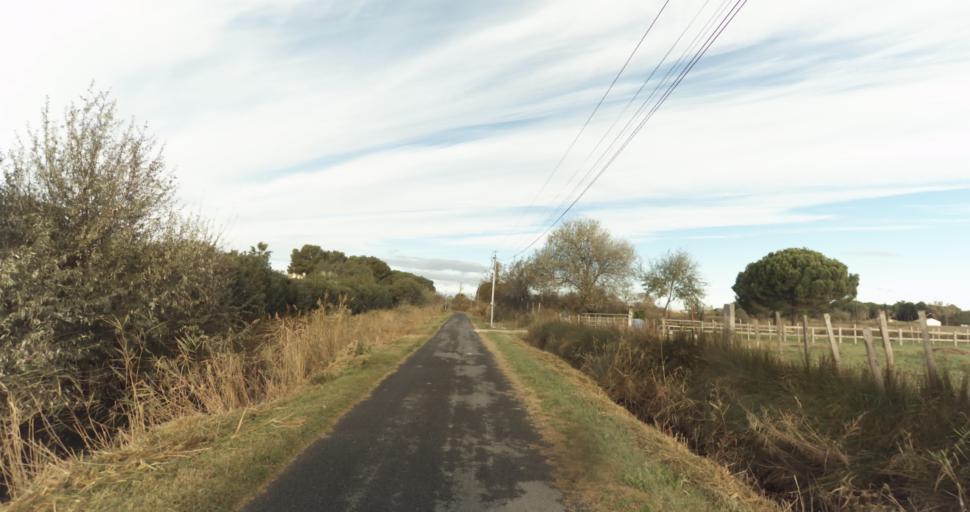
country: FR
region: Languedoc-Roussillon
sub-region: Departement du Gard
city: Aigues-Mortes
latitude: 43.5562
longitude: 4.2076
